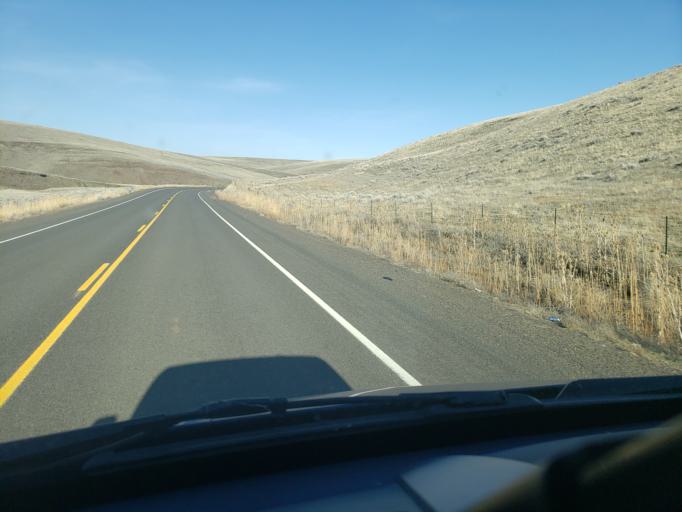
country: US
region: Oregon
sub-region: Umatilla County
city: Pilot Rock
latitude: 45.4644
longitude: -118.9258
